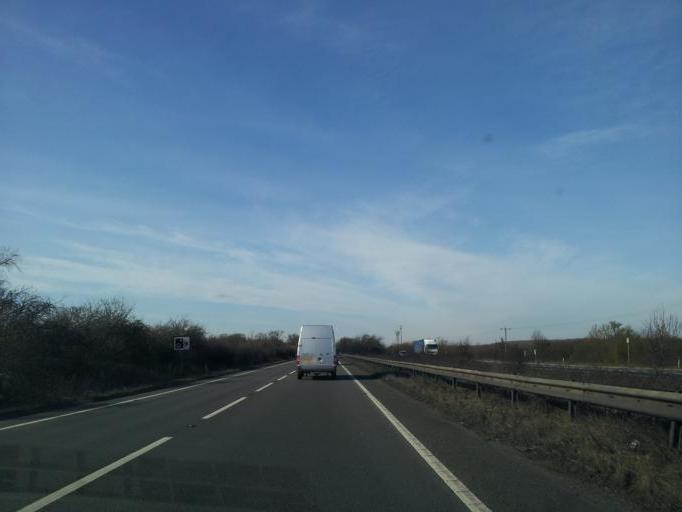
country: GB
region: England
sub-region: District of Rutland
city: Tickencote
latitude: 52.6943
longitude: -0.5671
